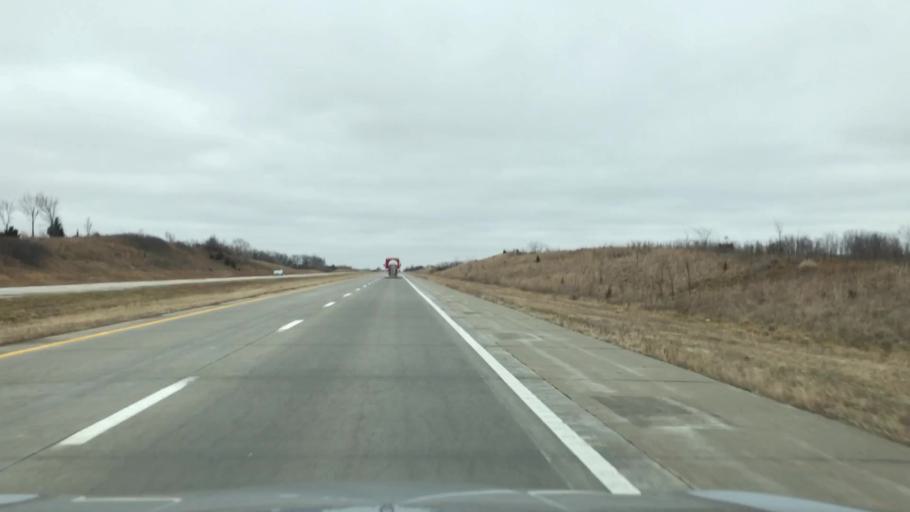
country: US
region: Missouri
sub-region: Caldwell County
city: Hamilton
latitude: 39.7345
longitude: -93.9590
